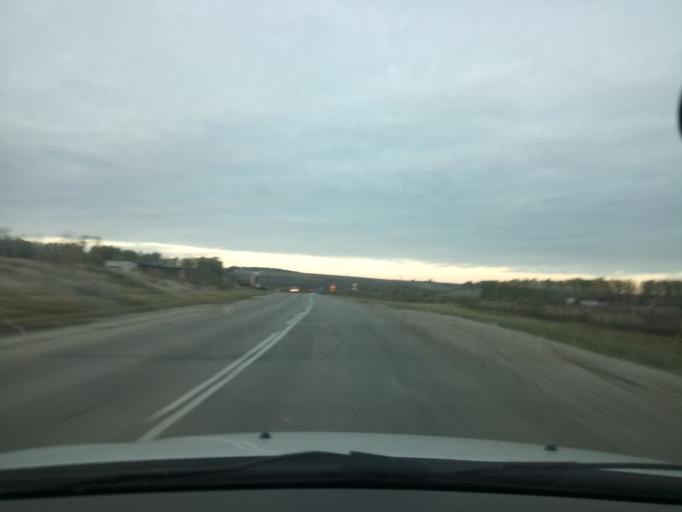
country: RU
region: Nizjnij Novgorod
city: Bol'shoye Murashkino
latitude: 55.8007
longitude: 44.7607
